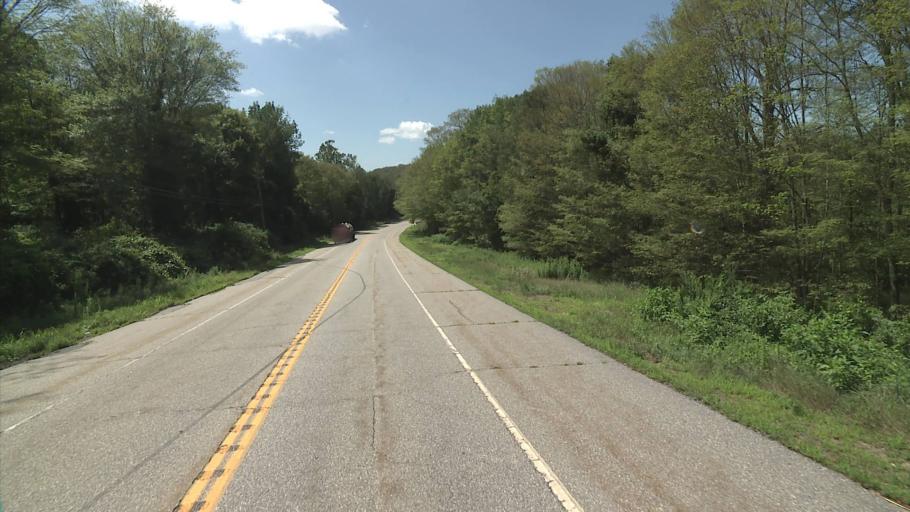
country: US
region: Connecticut
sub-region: Windham County
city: Plainfield Village
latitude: 41.6998
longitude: -71.9601
